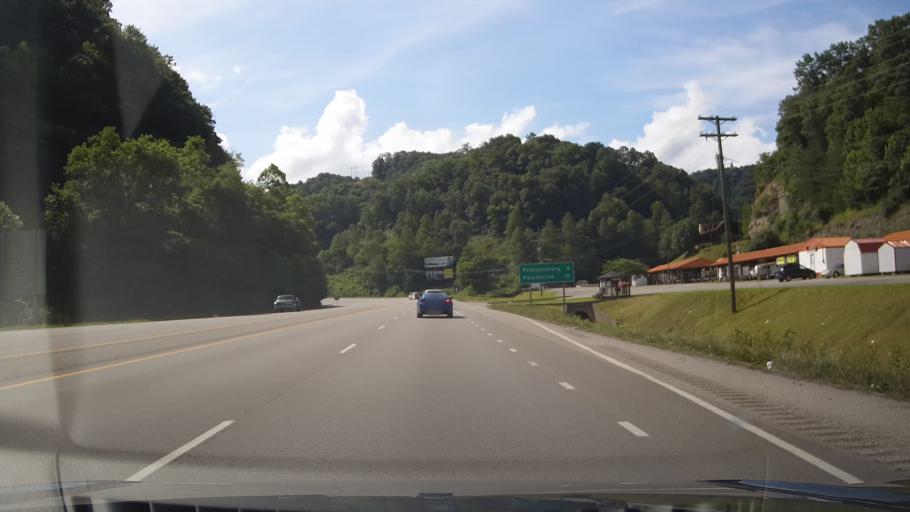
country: US
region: Kentucky
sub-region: Floyd County
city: Prestonsburg
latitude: 37.6402
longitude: -82.7558
